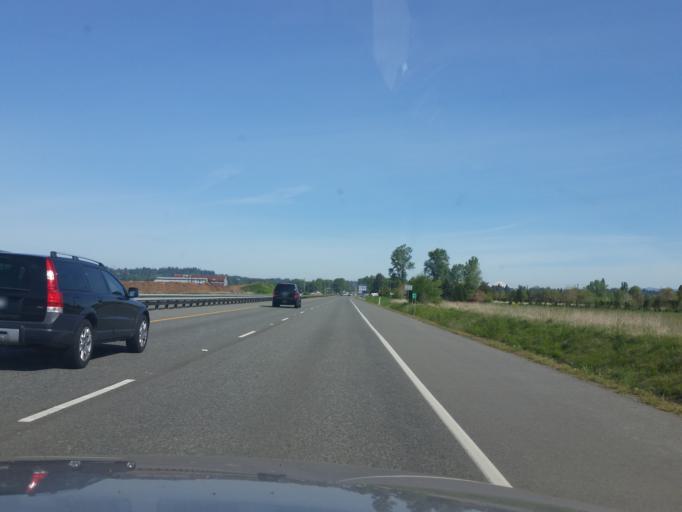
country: US
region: Washington
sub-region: Snohomish County
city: Snohomish
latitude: 47.8926
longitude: -122.1094
